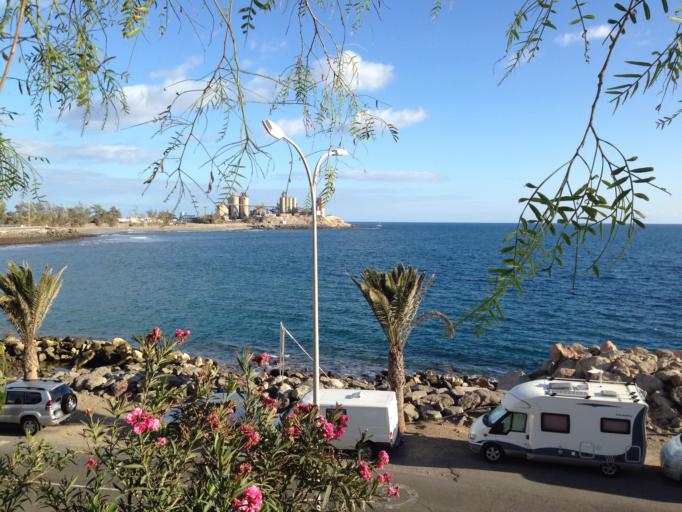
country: ES
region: Canary Islands
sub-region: Provincia de Las Palmas
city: Puerto Rico
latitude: 27.7559
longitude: -15.6823
